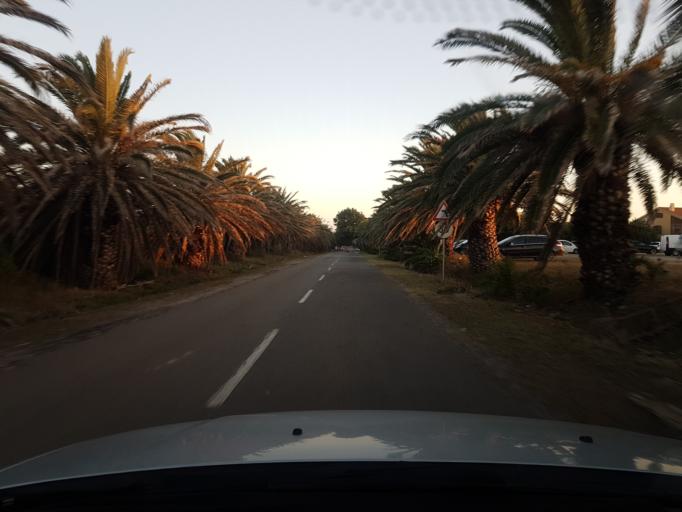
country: IT
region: Sardinia
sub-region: Provincia di Oristano
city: Riola Sardo
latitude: 40.0359
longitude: 8.3998
